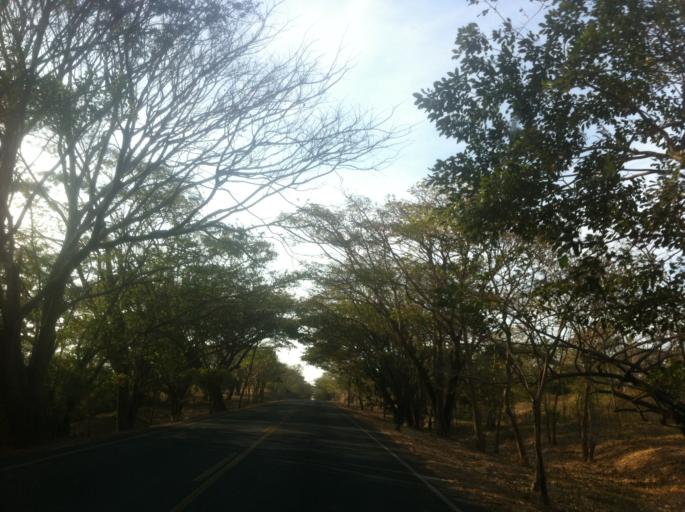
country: NI
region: Rivas
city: Cardenas
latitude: 11.2632
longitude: -85.6442
